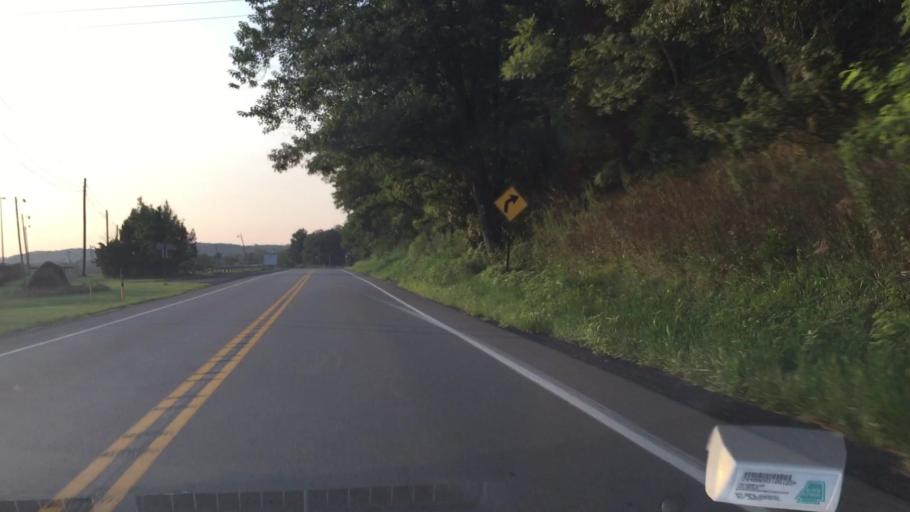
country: US
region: Pennsylvania
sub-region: Butler County
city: Evans City
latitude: 40.7448
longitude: -80.0344
